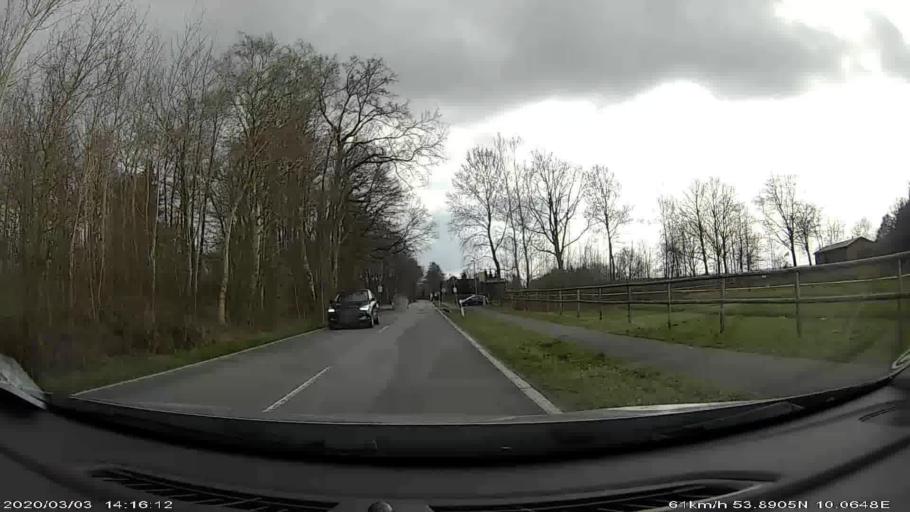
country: DE
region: Schleswig-Holstein
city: Hartenholm
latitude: 53.8901
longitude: 10.0651
